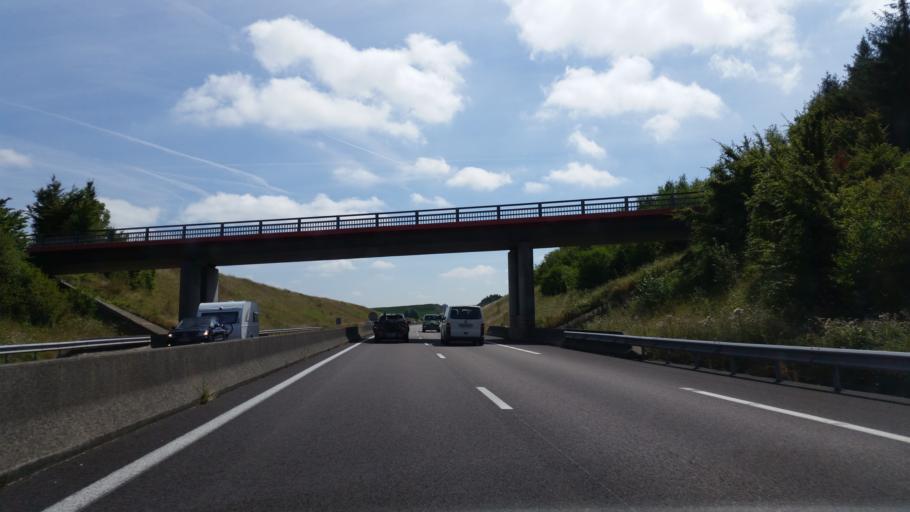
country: FR
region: Haute-Normandie
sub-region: Departement de la Seine-Maritime
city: Neufchatel-en-Bray
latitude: 49.7544
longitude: 1.4991
